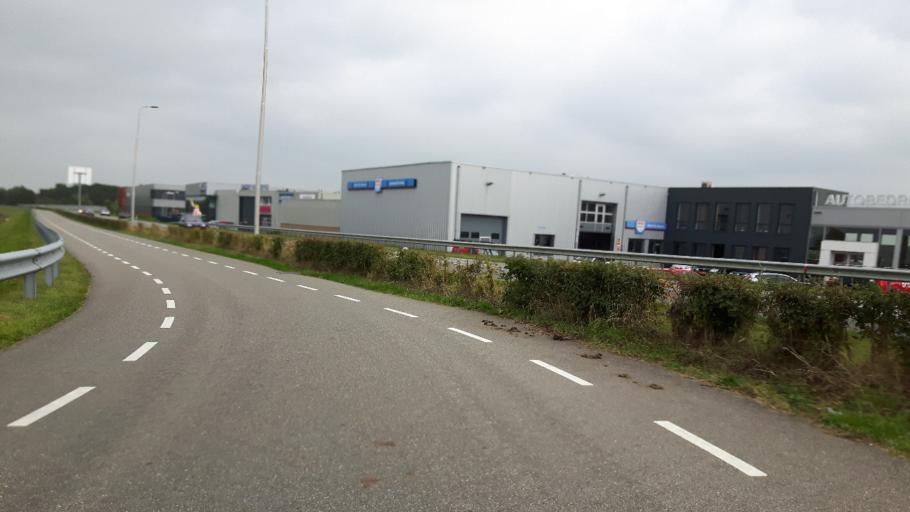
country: NL
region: South Holland
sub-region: Gemeente Gouda
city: Gouda
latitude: 51.9963
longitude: 4.6968
